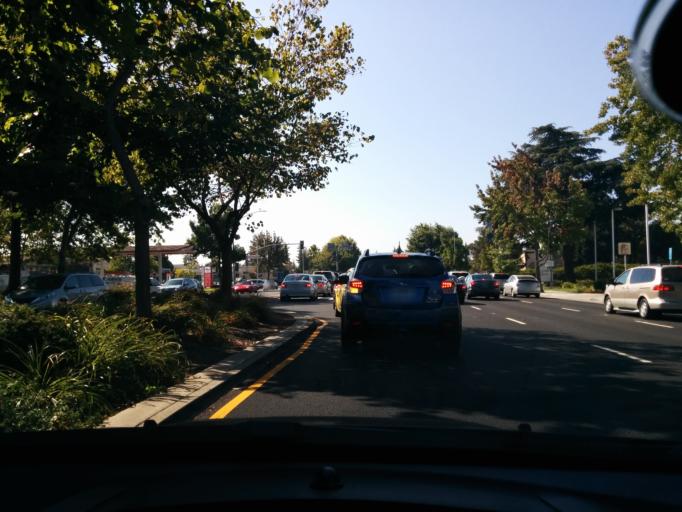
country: US
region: California
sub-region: Santa Clara County
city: Mountain View
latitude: 37.3799
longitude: -122.0719
